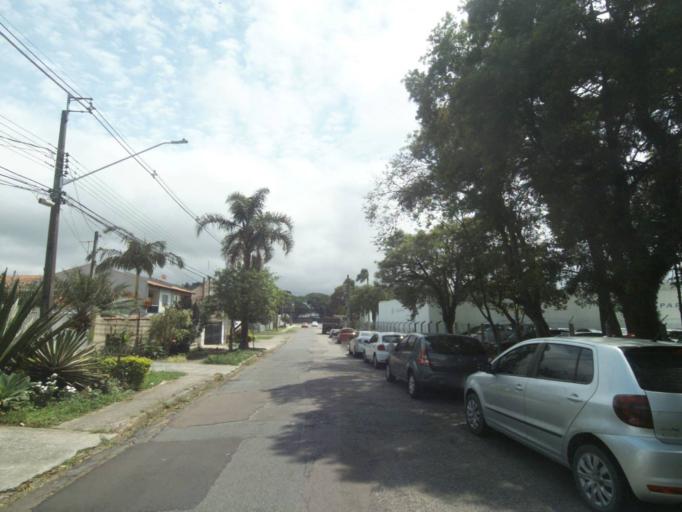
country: BR
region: Parana
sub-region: Pinhais
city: Pinhais
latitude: -25.4305
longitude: -49.2237
